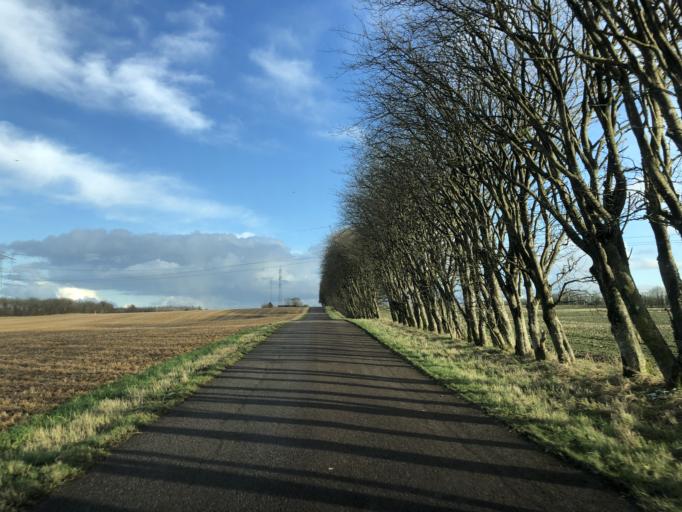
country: DK
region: Central Jutland
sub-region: Viborg Kommune
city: Viborg
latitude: 56.5036
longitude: 9.4280
